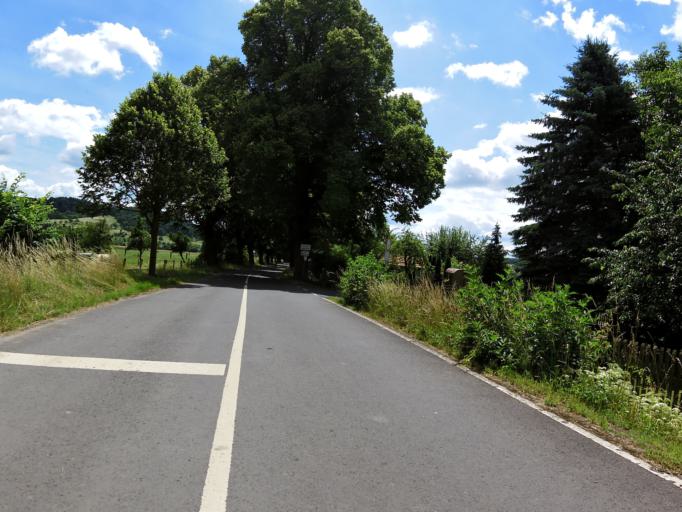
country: DE
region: Thuringia
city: Lauchroden
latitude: 51.0040
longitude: 10.1600
